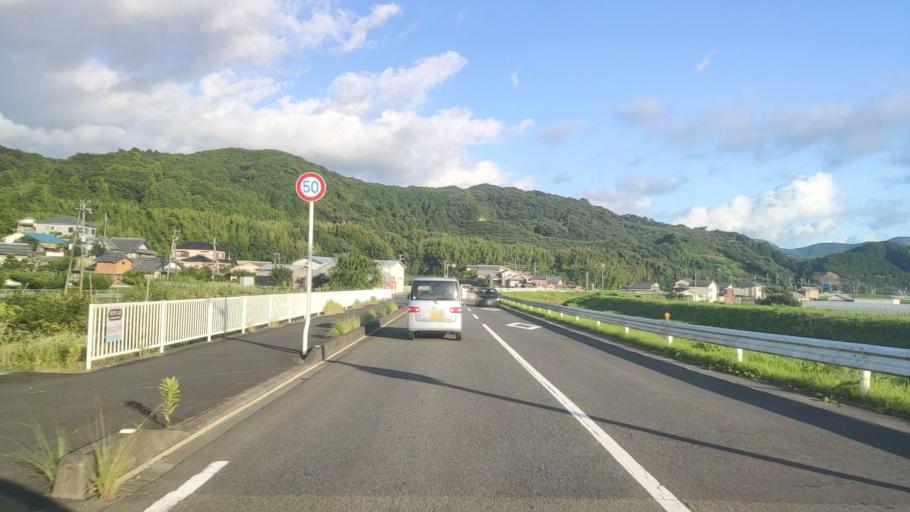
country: JP
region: Wakayama
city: Tanabe
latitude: 33.7179
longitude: 135.4466
